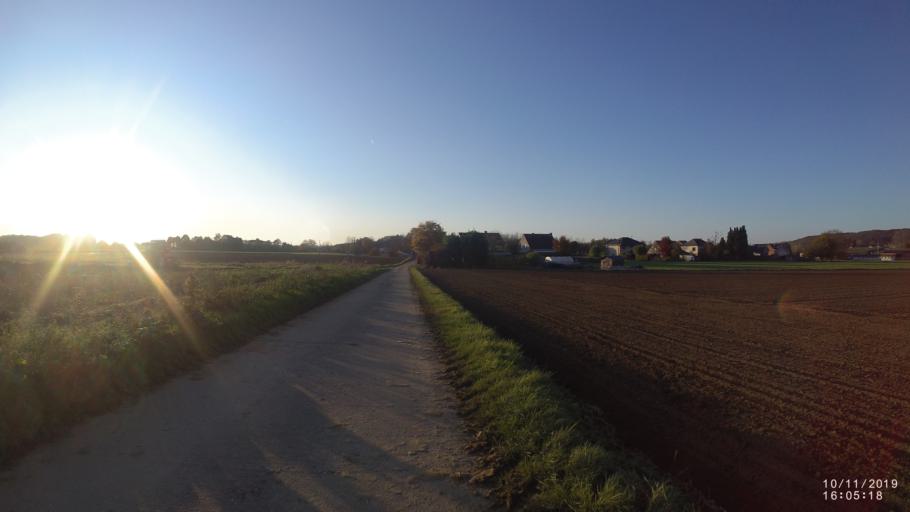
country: BE
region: Flanders
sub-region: Provincie Vlaams-Brabant
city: Lubbeek
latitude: 50.9012
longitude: 4.8608
